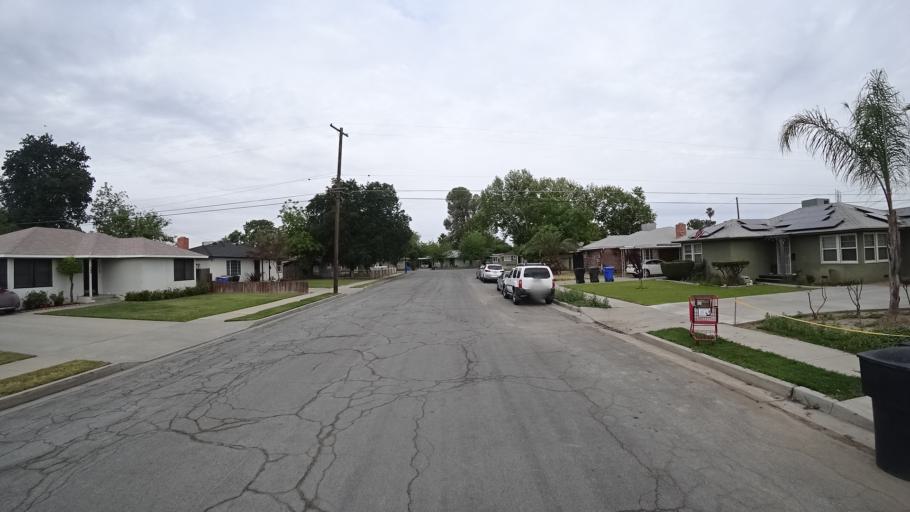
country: US
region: California
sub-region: Kings County
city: Hanford
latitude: 36.3391
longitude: -119.6555
